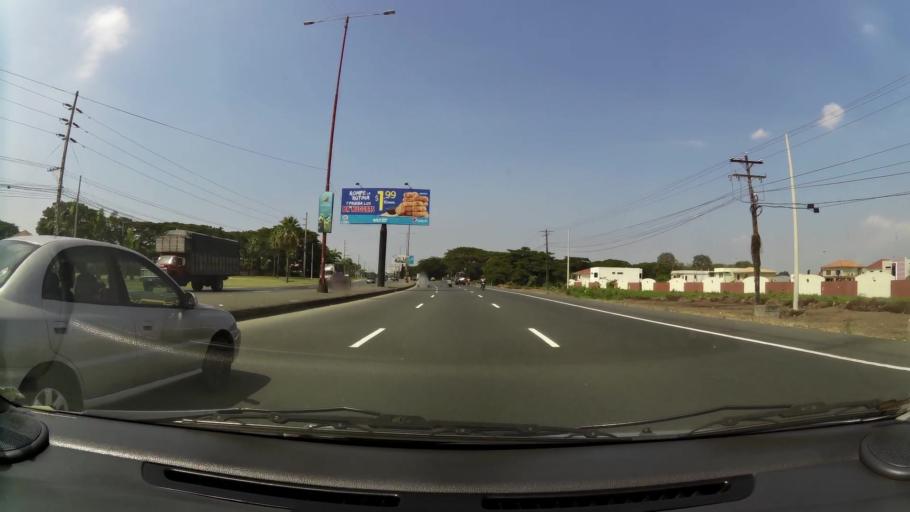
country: EC
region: Guayas
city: Eloy Alfaro
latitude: -2.0521
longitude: -79.8956
